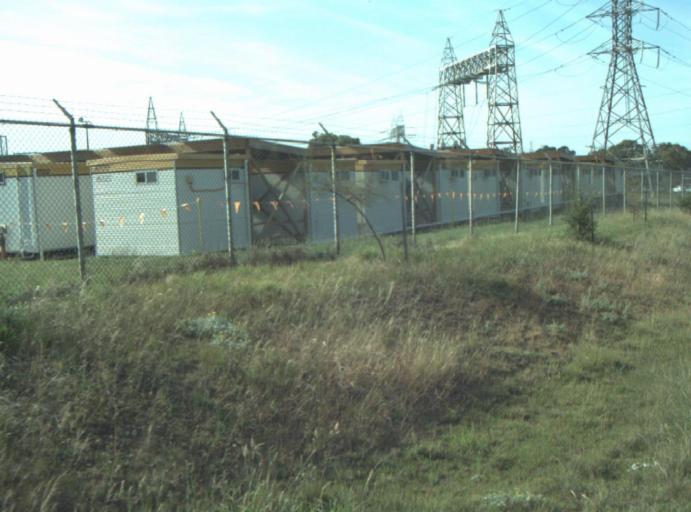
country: AU
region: Victoria
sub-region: Greater Geelong
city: Leopold
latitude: -38.1814
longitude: 144.4475
